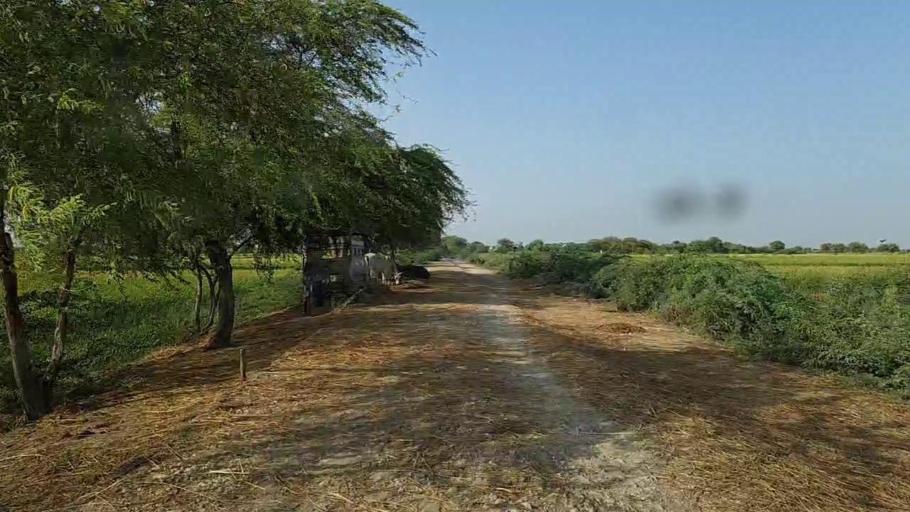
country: PK
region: Sindh
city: Bulri
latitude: 24.7777
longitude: 68.4335
